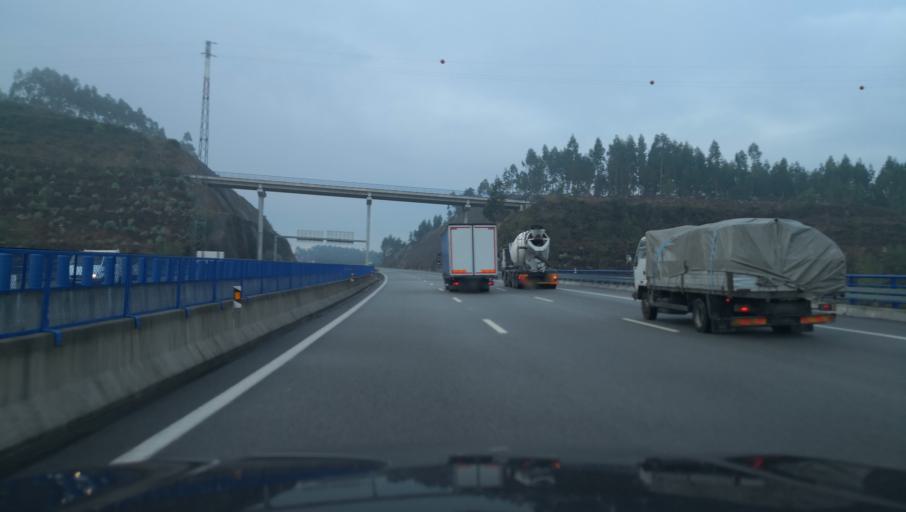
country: PT
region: Porto
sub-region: Paredes
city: Recarei
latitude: 41.1268
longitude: -8.4320
